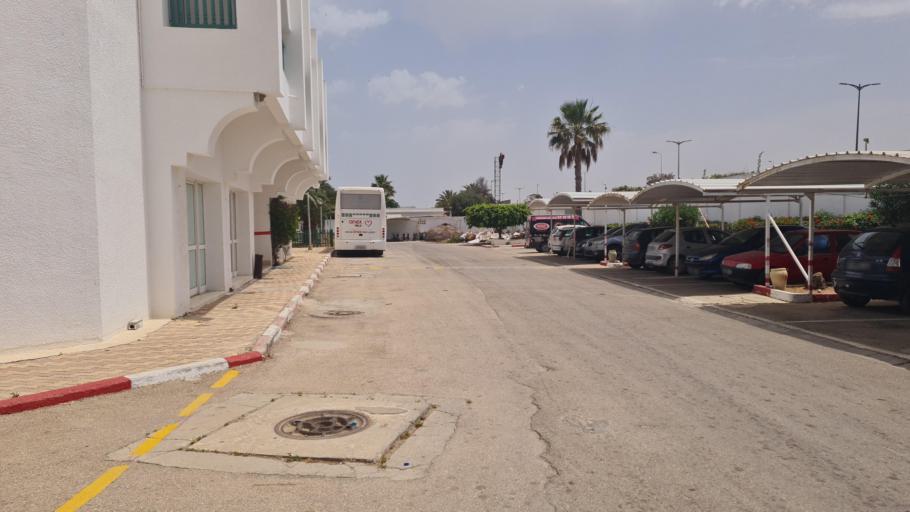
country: TN
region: Susah
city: Port el Kantaoui
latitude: 35.9030
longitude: 10.5833
